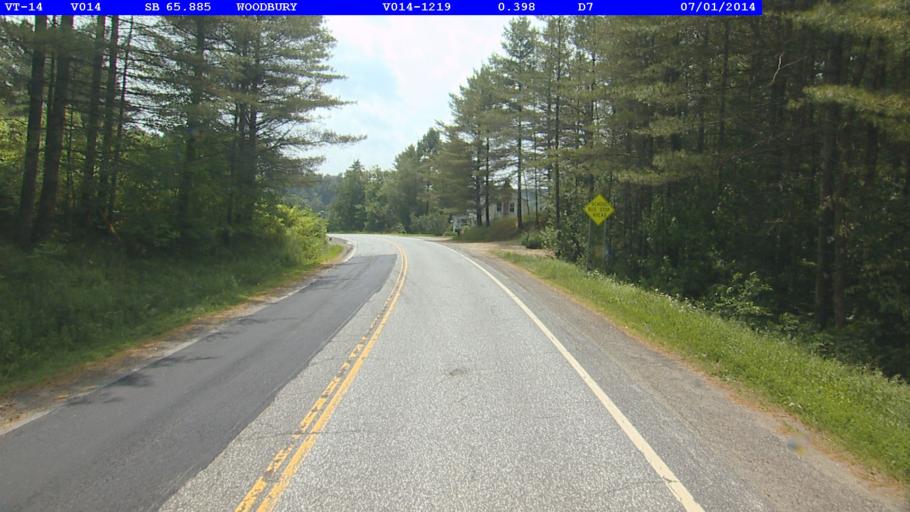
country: US
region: Vermont
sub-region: Caledonia County
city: Hardwick
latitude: 44.4018
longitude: -72.4128
